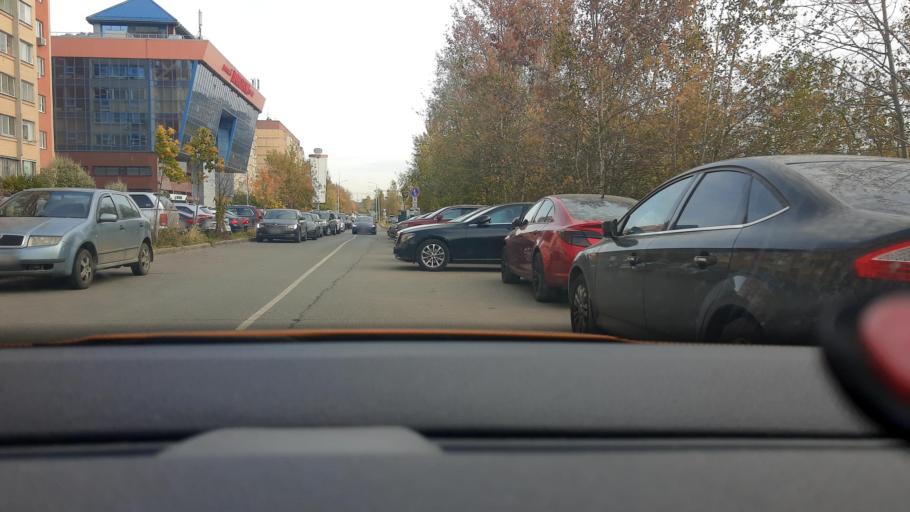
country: RU
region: Moskovskaya
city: Krasnogorsk
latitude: 55.8279
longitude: 37.2966
